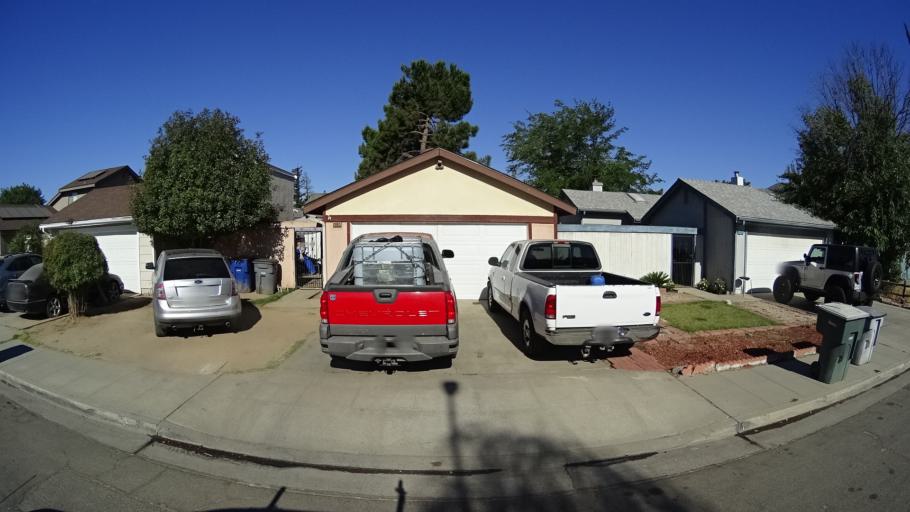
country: US
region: California
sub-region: Fresno County
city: West Park
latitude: 36.7772
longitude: -119.8561
